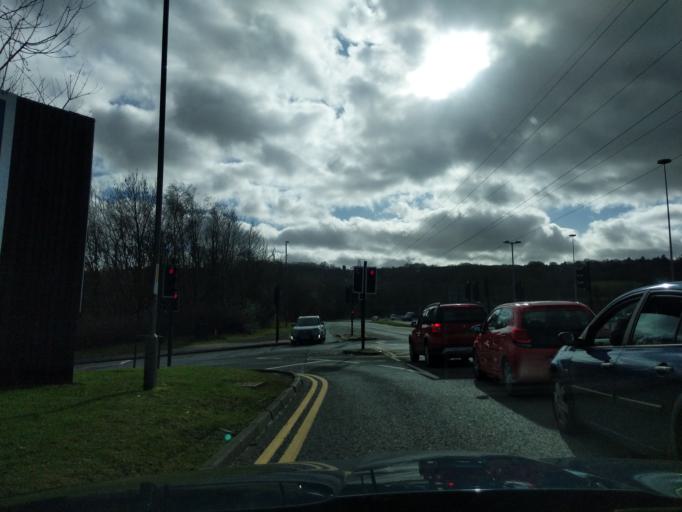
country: GB
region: England
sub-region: Gateshead
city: Whickham
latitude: 54.9566
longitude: -1.6625
